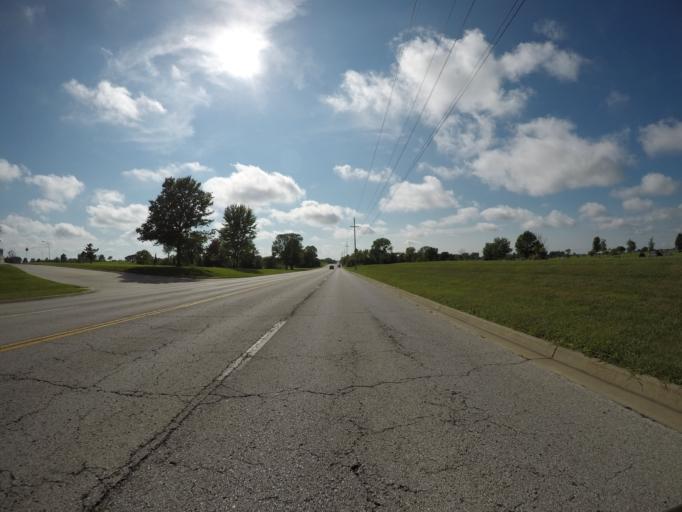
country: US
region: Kansas
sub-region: Leavenworth County
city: Basehor
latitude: 39.1287
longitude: -94.8742
